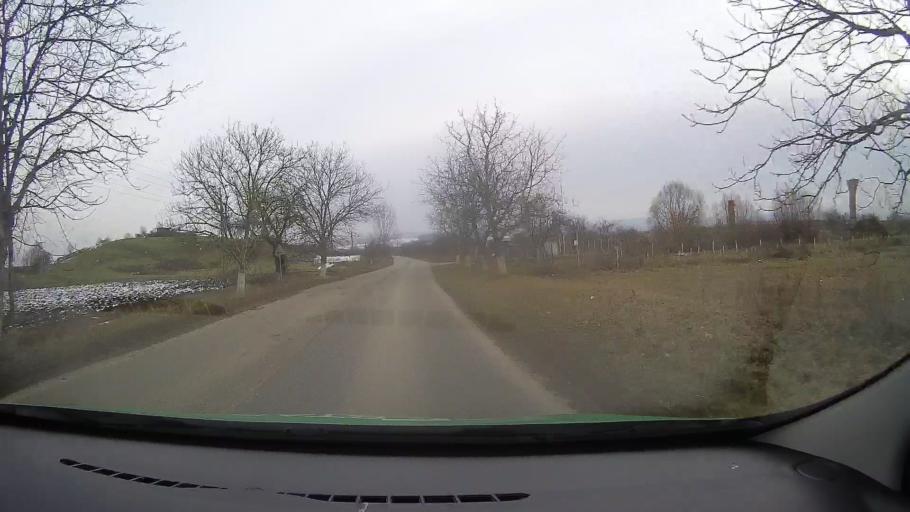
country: RO
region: Hunedoara
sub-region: Comuna Romos
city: Romos
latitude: 45.8804
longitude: 23.2571
